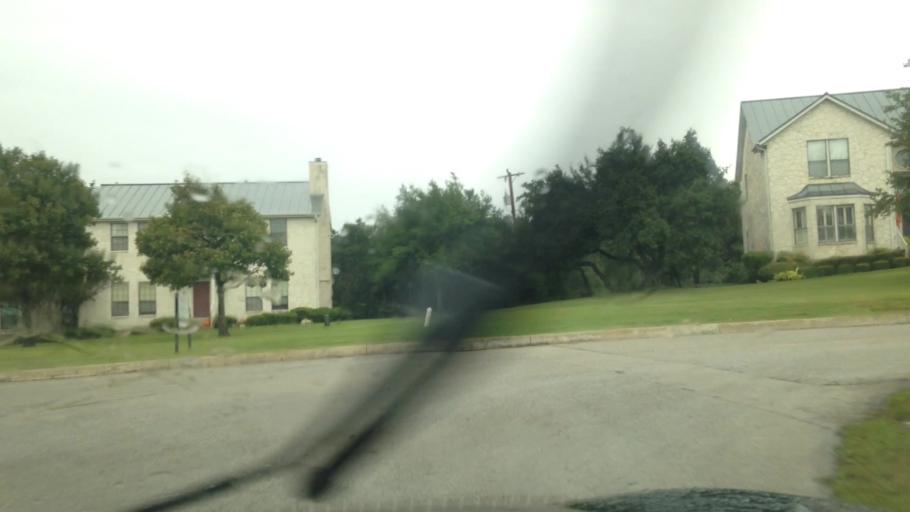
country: US
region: Texas
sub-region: Bexar County
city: Cross Mountain
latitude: 29.6400
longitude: -98.6042
